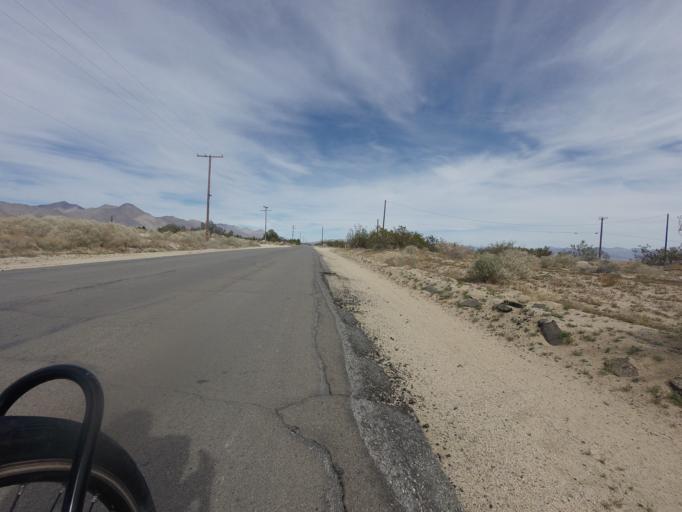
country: US
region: California
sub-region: Kern County
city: Inyokern
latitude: 35.7245
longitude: -117.8353
